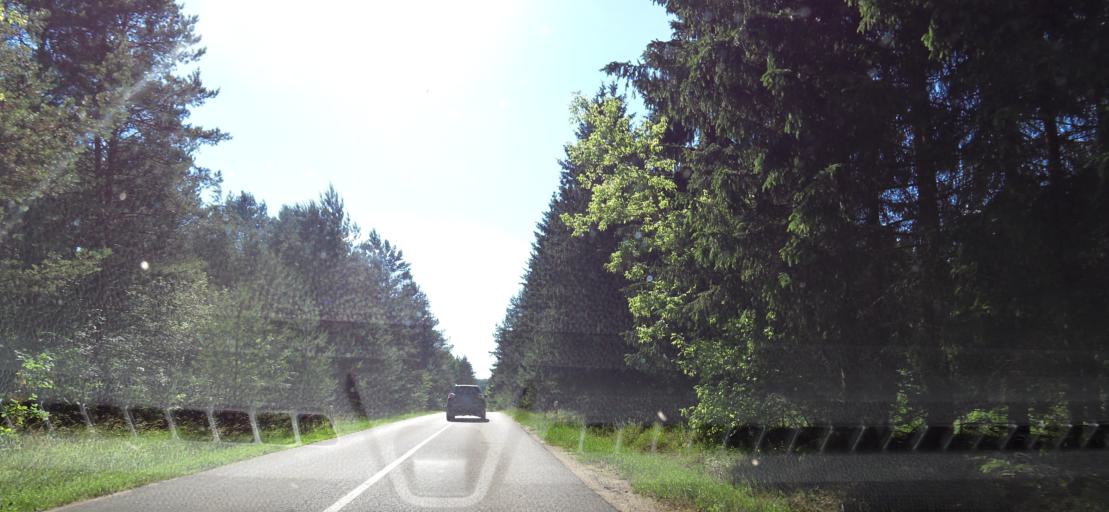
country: LT
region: Vilnius County
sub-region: Vilnius
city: Vilnius
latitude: 54.7493
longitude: 25.3131
